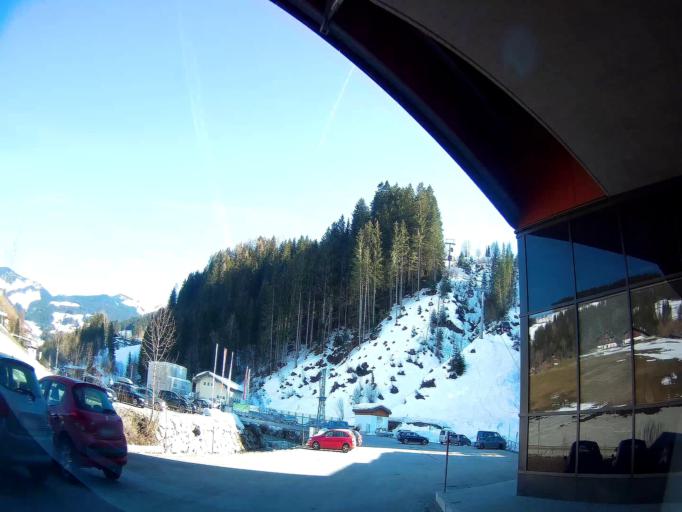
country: AT
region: Salzburg
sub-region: Politischer Bezirk Zell am See
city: Maria Alm am Steinernen Meer
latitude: 47.3903
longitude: 12.9080
